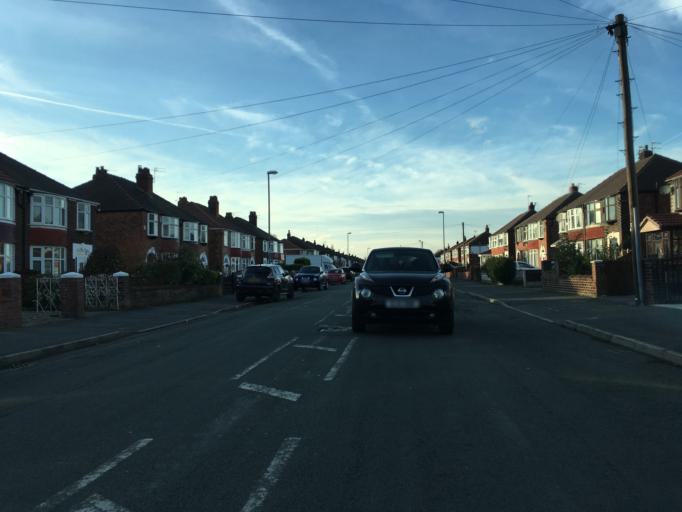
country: GB
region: England
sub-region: Manchester
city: Chorlton cum Hardy
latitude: 53.4460
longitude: -2.2631
